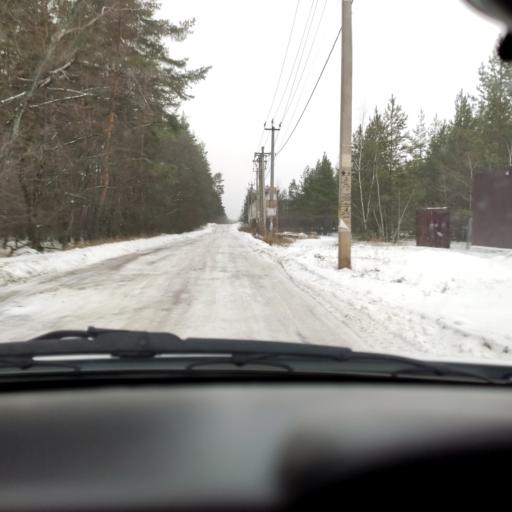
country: RU
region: Voronezj
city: Ramon'
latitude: 51.8862
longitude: 39.2551
